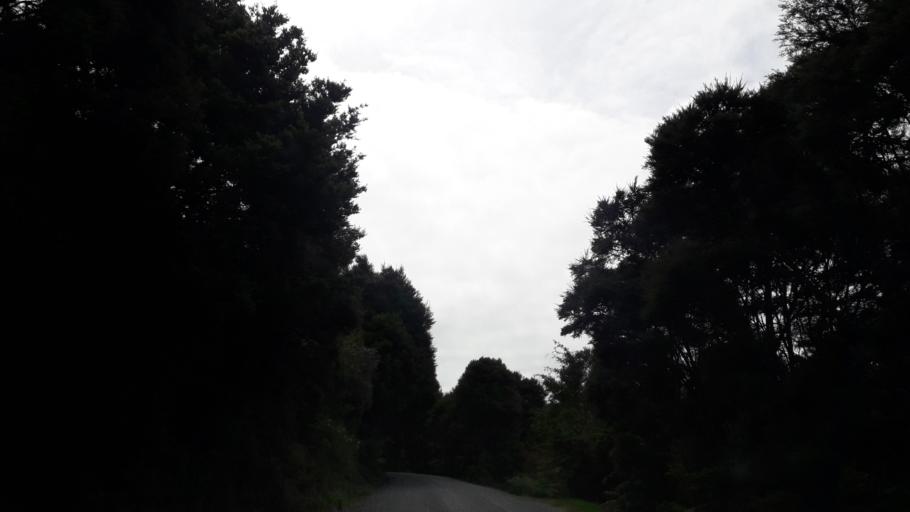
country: NZ
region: Northland
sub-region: Far North District
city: Taipa
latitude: -35.0311
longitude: 173.5626
